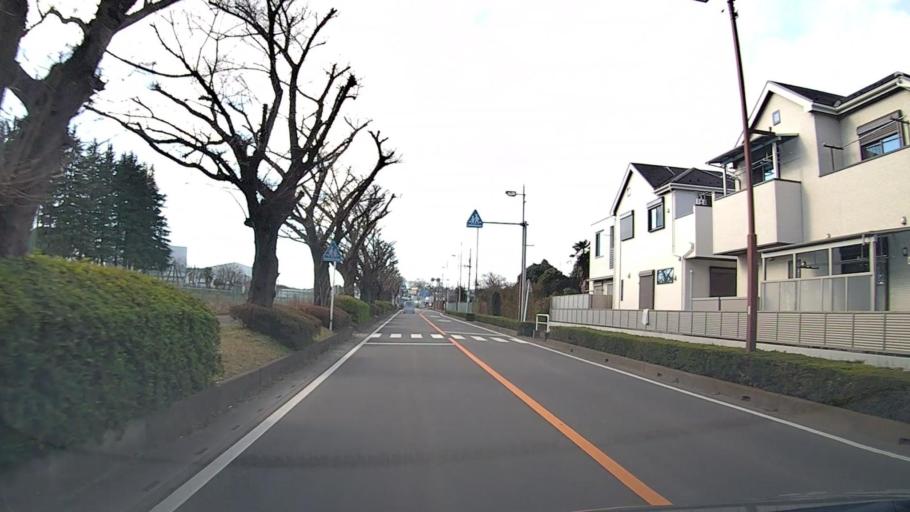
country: JP
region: Saitama
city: Asaka
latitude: 35.7777
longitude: 139.5754
